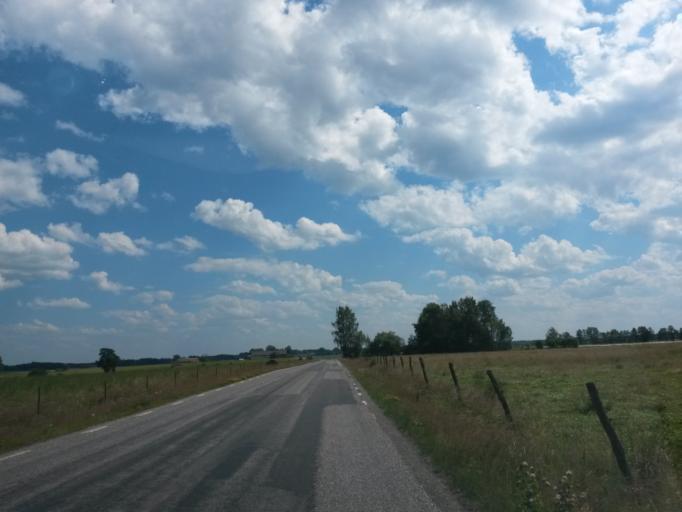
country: SE
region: Vaestra Goetaland
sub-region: Essunga Kommun
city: Nossebro
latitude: 58.1512
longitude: 12.7532
